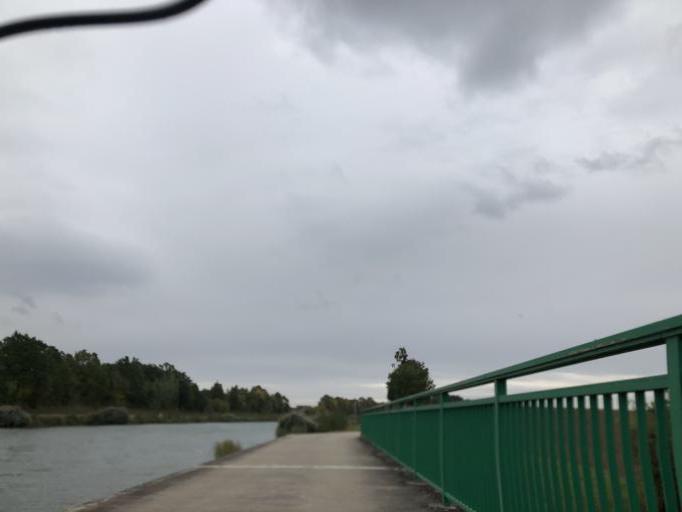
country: DE
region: Bavaria
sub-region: Regierungsbezirk Mittelfranken
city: Obermichelbach
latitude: 49.5392
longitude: 10.9679
